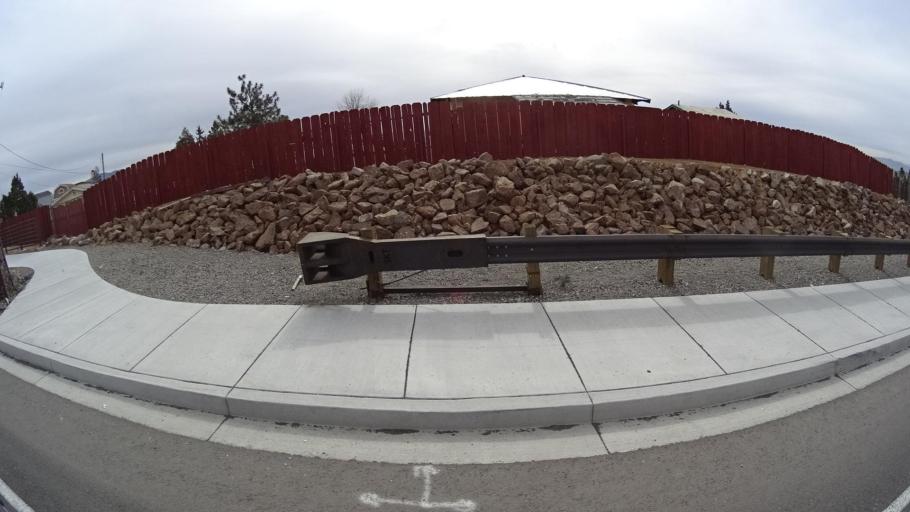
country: US
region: Nevada
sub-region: Washoe County
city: Sun Valley
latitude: 39.6081
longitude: -119.7802
